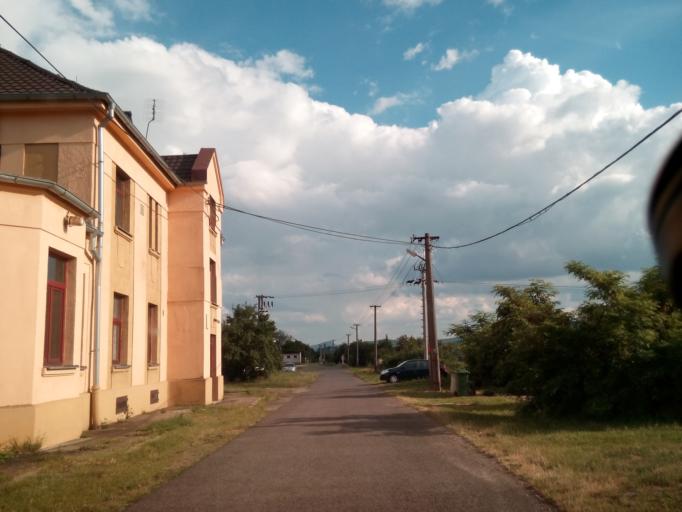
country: SK
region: Kosicky
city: Secovce
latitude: 48.5819
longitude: 21.5790
